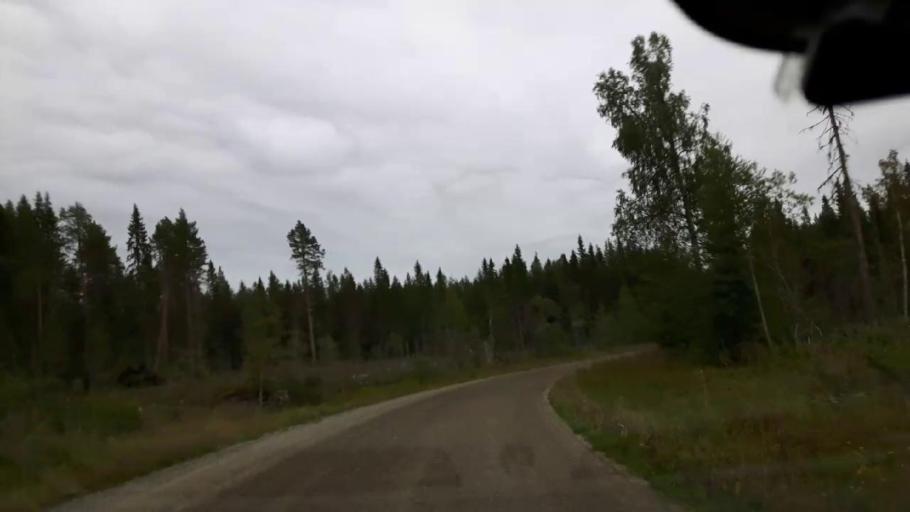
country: SE
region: Jaemtland
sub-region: Braecke Kommun
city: Braecke
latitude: 62.9802
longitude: 15.4016
